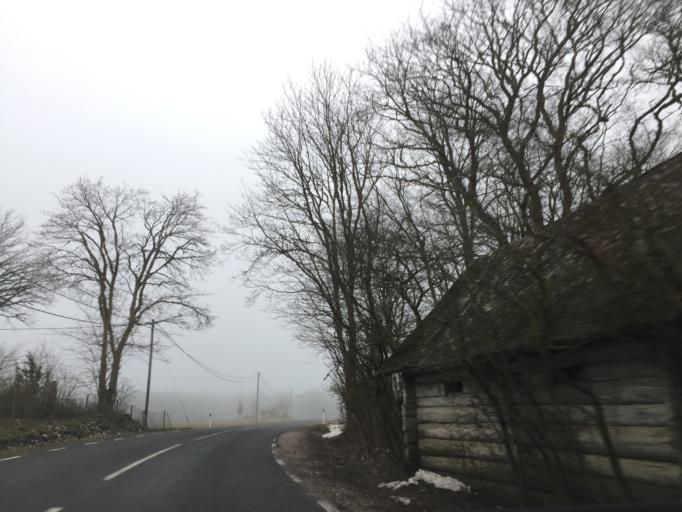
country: EE
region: Saare
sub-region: Kuressaare linn
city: Kuressaare
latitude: 58.4659
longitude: 22.0090
